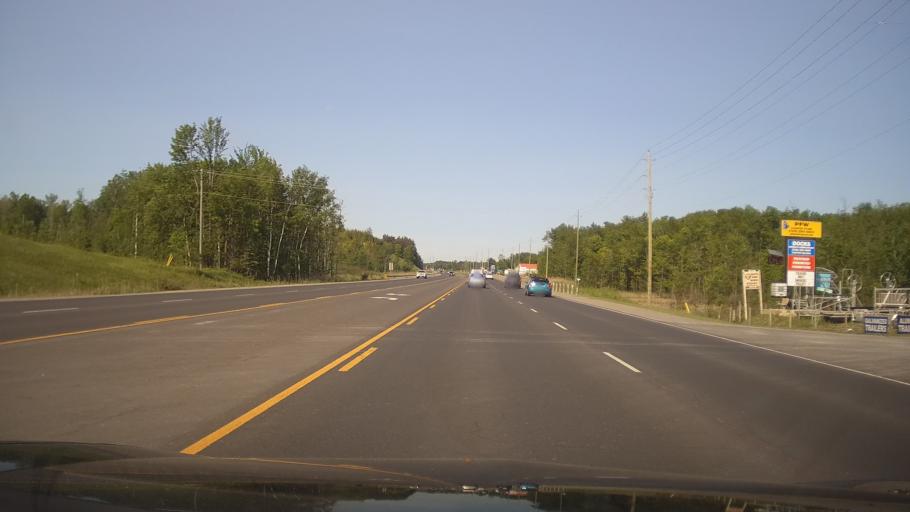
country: CA
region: Ontario
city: Peterborough
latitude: 44.3107
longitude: -78.2259
